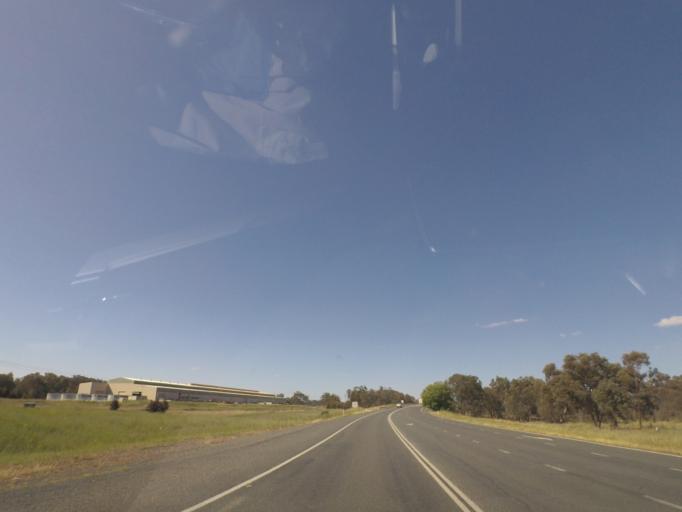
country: AU
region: New South Wales
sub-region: Albury Municipality
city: Lavington
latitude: -36.0056
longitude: 146.9855
